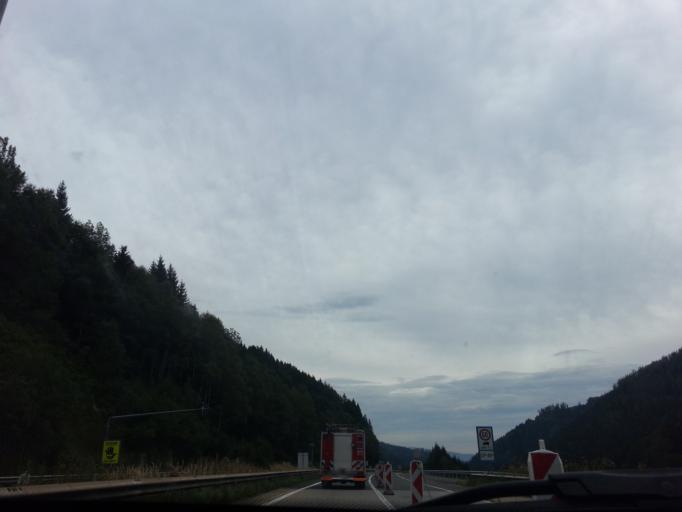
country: AT
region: Styria
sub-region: Politischer Bezirk Graz-Umgebung
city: Ubelbach
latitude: 47.2481
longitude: 15.1636
